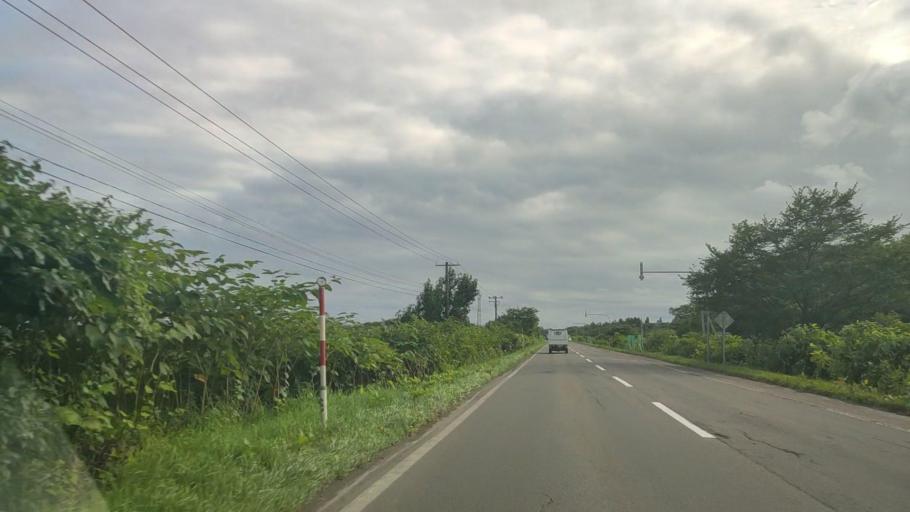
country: JP
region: Hokkaido
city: Niseko Town
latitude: 42.4611
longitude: 140.3369
